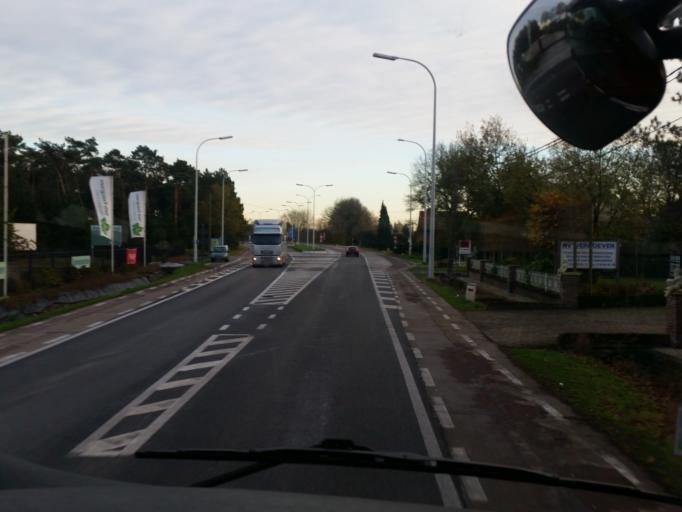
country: BE
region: Flanders
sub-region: Provincie Antwerpen
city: Oud-Turnhout
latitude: 51.2983
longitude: 5.0274
